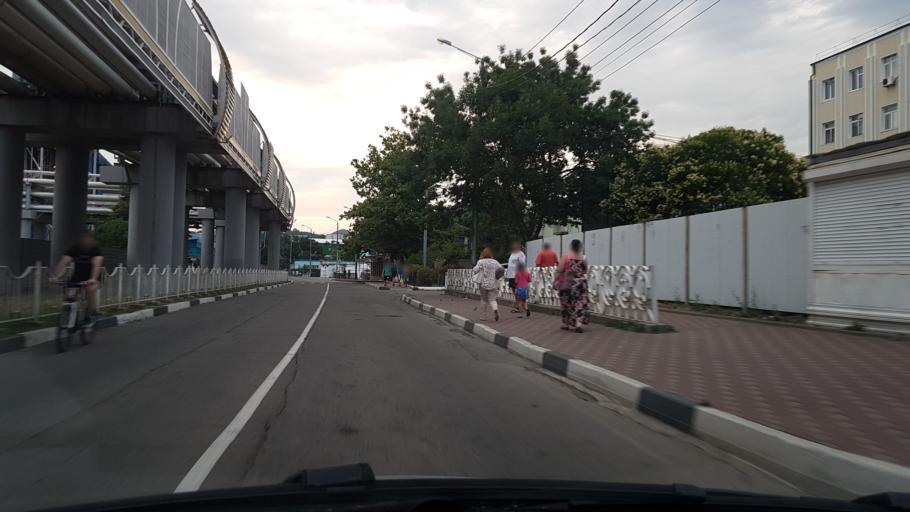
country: RU
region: Krasnodarskiy
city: Tuapse
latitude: 44.0913
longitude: 39.0811
